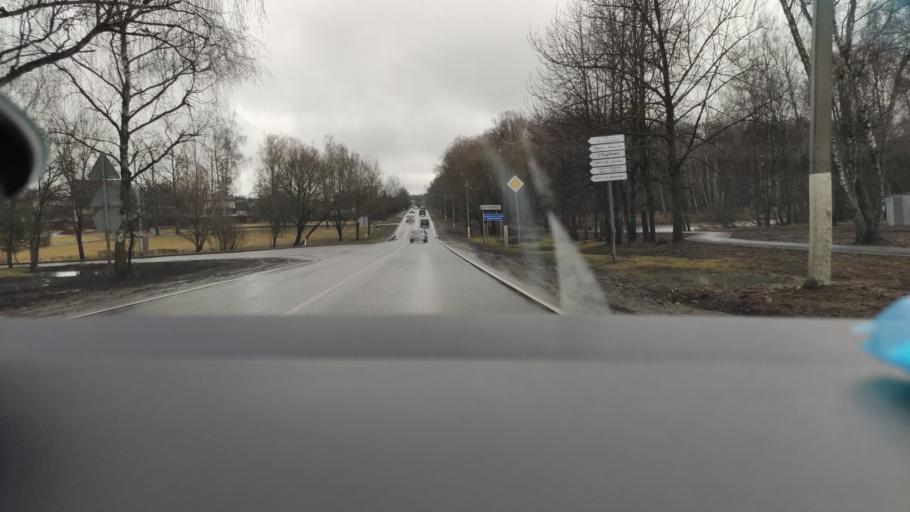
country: RU
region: Moskovskaya
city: Troitsk
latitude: 55.3107
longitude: 37.1746
